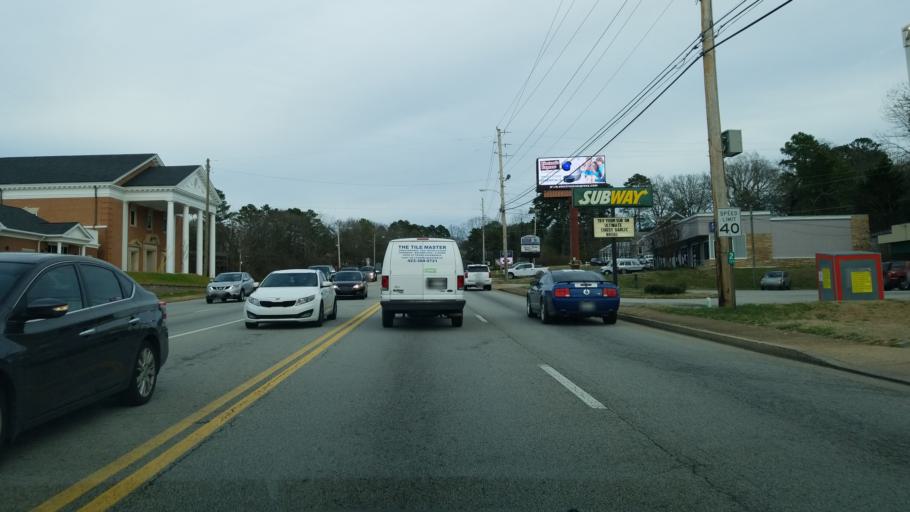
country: US
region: Tennessee
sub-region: Hamilton County
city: East Brainerd
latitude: 35.0179
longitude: -85.1732
